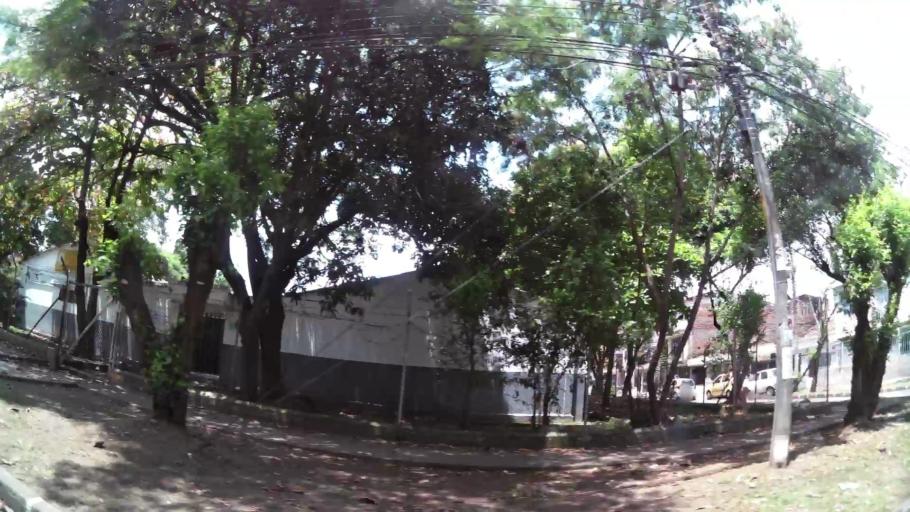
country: CO
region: Valle del Cauca
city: Cali
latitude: 3.4431
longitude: -76.4983
